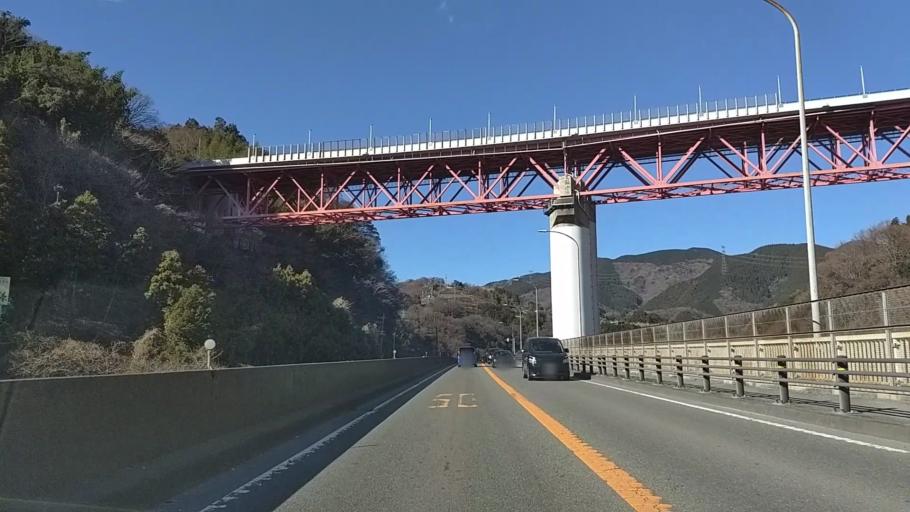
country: JP
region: Shizuoka
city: Gotemba
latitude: 35.3691
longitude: 139.0364
